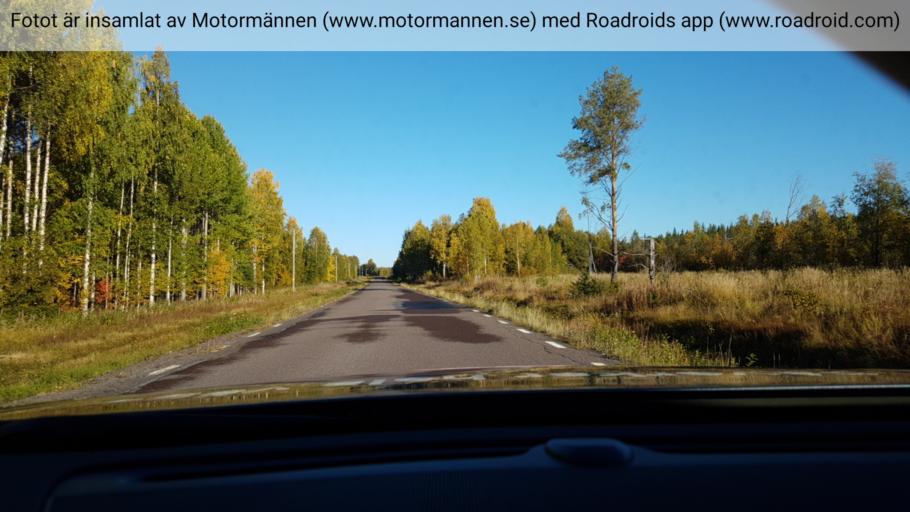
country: SE
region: Norrbotten
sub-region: Bodens Kommun
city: Boden
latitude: 66.0865
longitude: 21.3842
